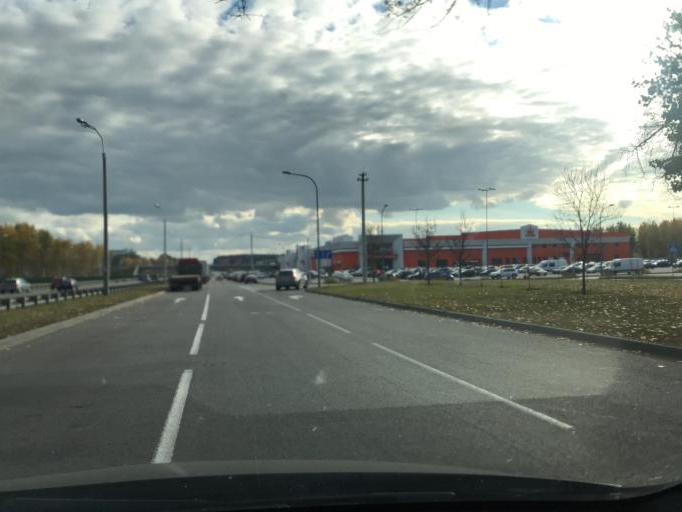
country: BY
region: Minsk
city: Borovlyany
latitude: 53.9390
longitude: 27.6735
